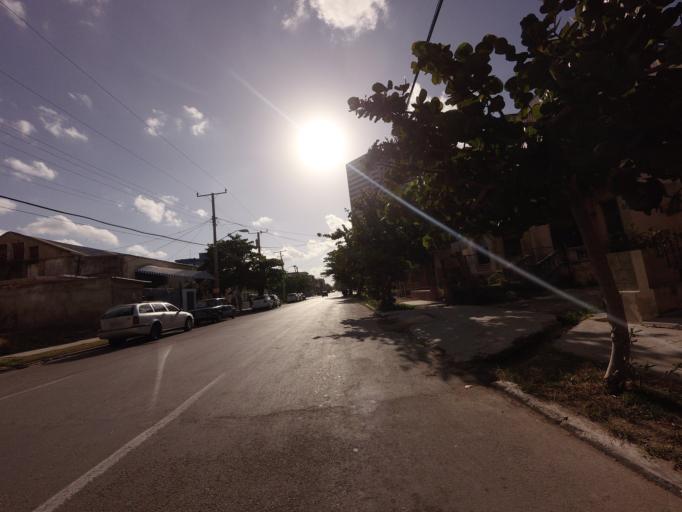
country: CU
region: La Habana
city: Havana
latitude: 23.1402
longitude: -82.4012
